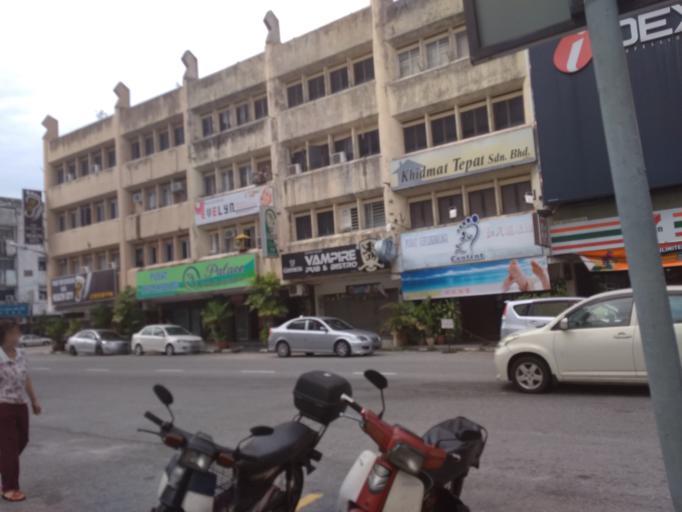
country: MY
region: Perak
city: Ipoh
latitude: 4.5974
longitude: 101.0869
